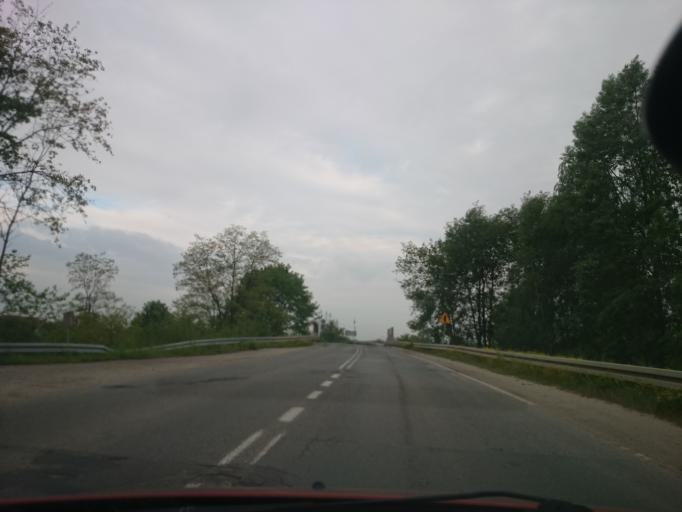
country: PL
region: Opole Voivodeship
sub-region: Powiat opolski
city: Czarnowasy
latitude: 50.7386
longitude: 17.8855
